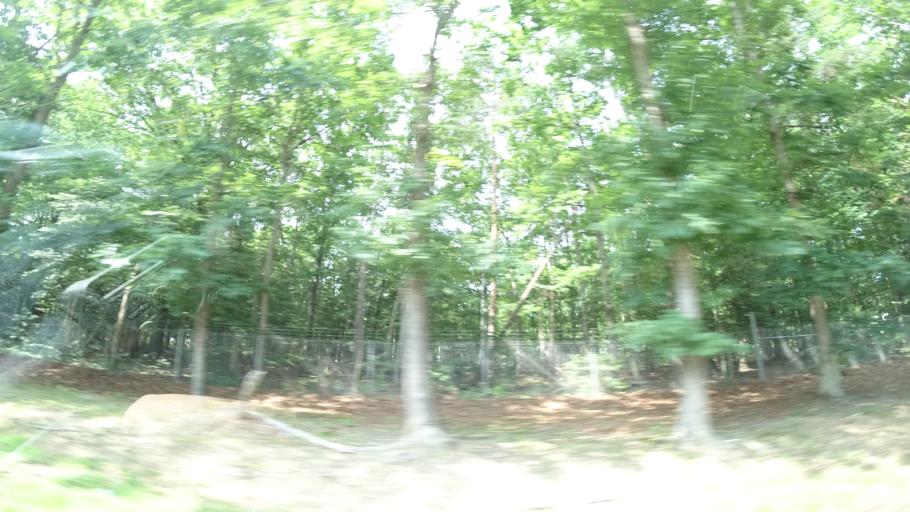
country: US
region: Virginia
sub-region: Spotsylvania County
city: Spotsylvania Courthouse
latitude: 38.1390
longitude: -77.5488
